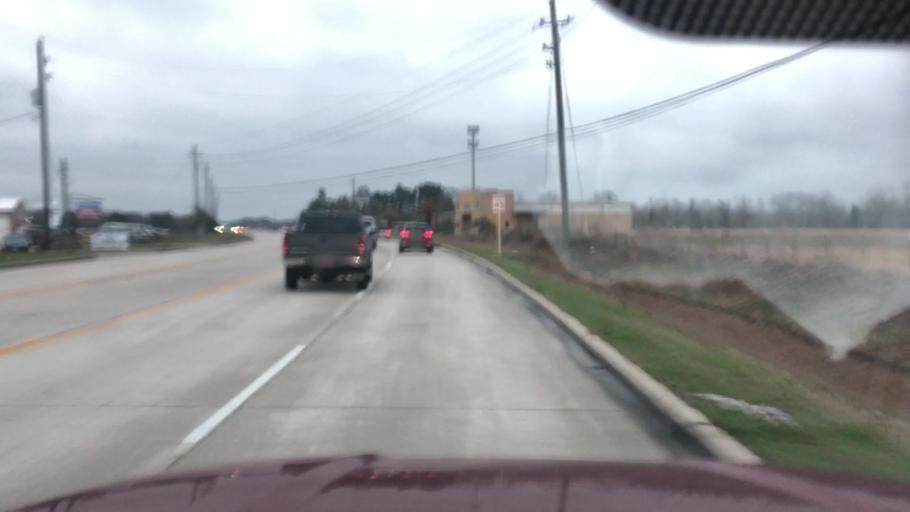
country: US
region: Texas
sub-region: Harris County
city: Tomball
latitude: 30.0483
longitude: -95.5388
